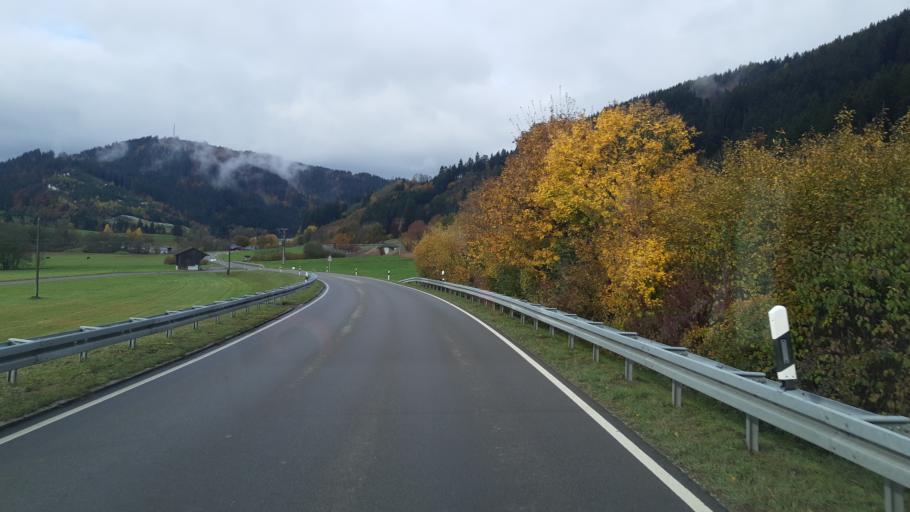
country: DE
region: Bavaria
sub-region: Swabia
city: Weitnau
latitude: 47.6415
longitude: 10.1085
